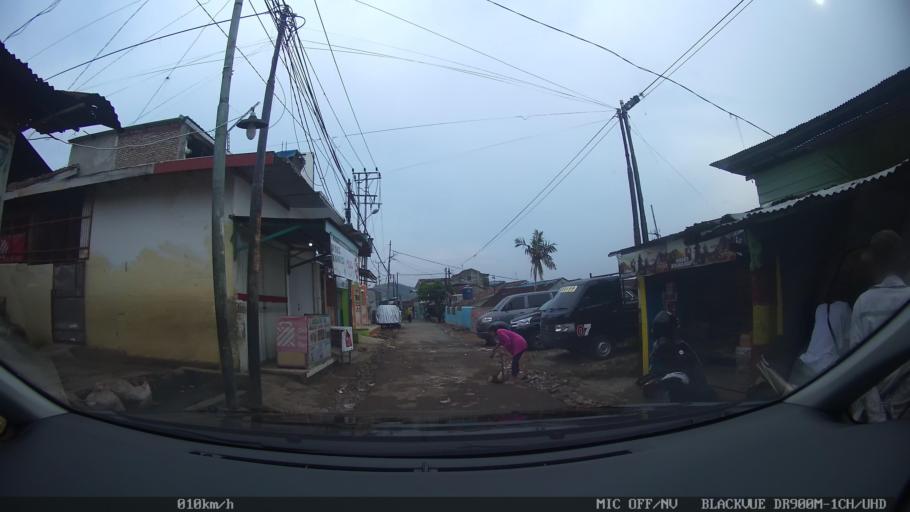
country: ID
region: Lampung
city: Bandarlampung
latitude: -5.4139
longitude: 105.2508
